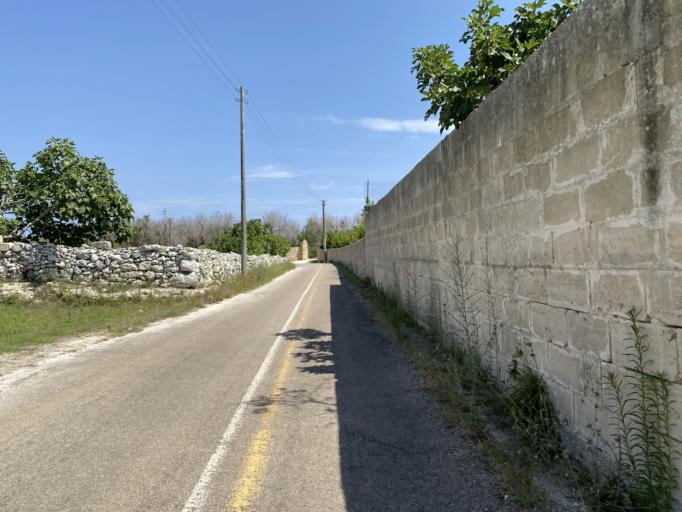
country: IT
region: Apulia
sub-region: Provincia di Lecce
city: Sanarica
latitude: 40.0942
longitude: 18.3529
